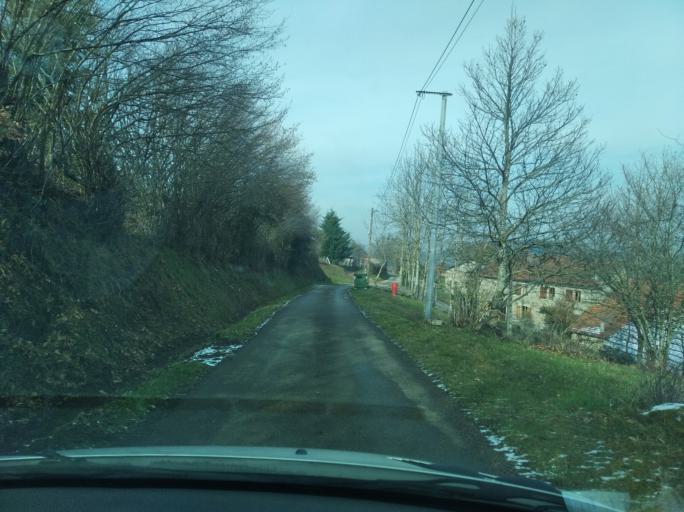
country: FR
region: Auvergne
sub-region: Departement de l'Allier
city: Le Mayet-de-Montagne
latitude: 46.1445
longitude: 3.7559
